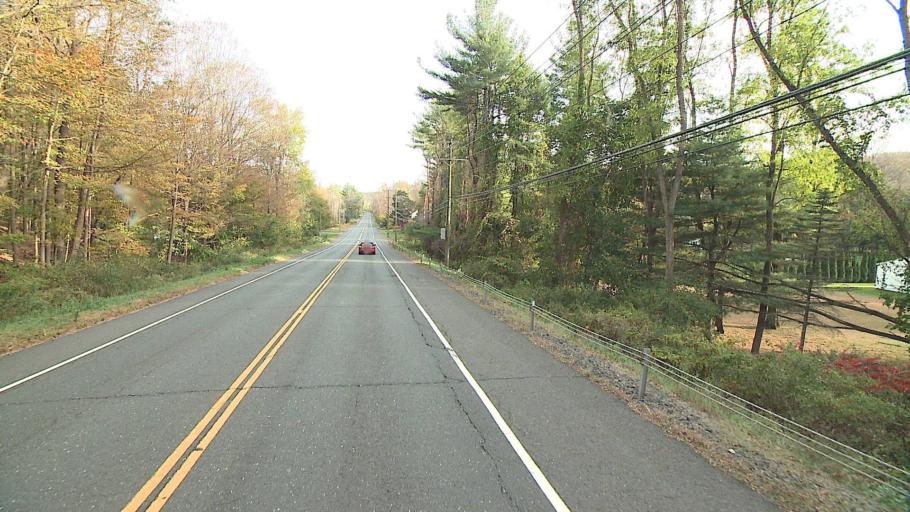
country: US
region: Connecticut
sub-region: Hartford County
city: Collinsville
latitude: 41.8463
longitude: -72.9437
